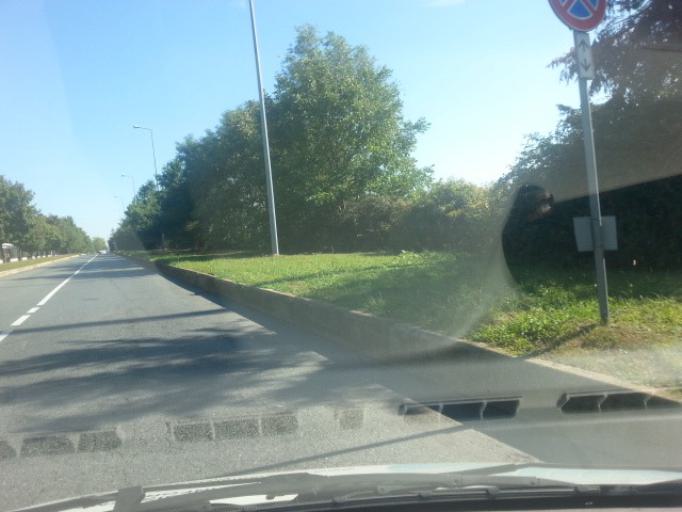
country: IT
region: Piedmont
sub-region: Provincia di Torino
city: Tetti Neirotti
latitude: 45.0356
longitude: 7.5564
